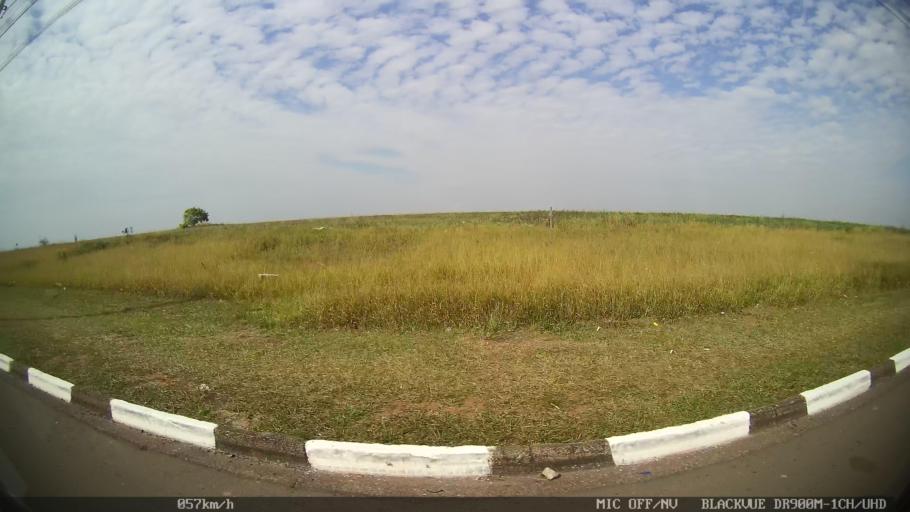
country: BR
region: Sao Paulo
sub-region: Paulinia
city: Paulinia
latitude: -22.7907
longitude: -47.1702
